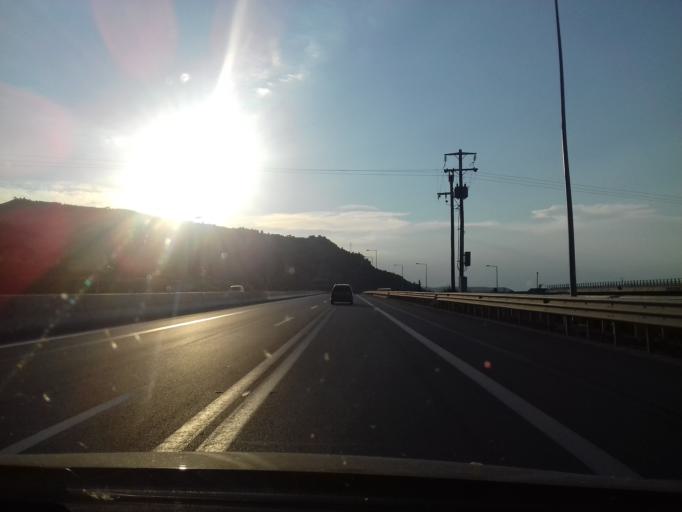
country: GR
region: West Greece
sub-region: Nomos Achaias
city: Aiyira
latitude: 38.1312
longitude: 22.4046
